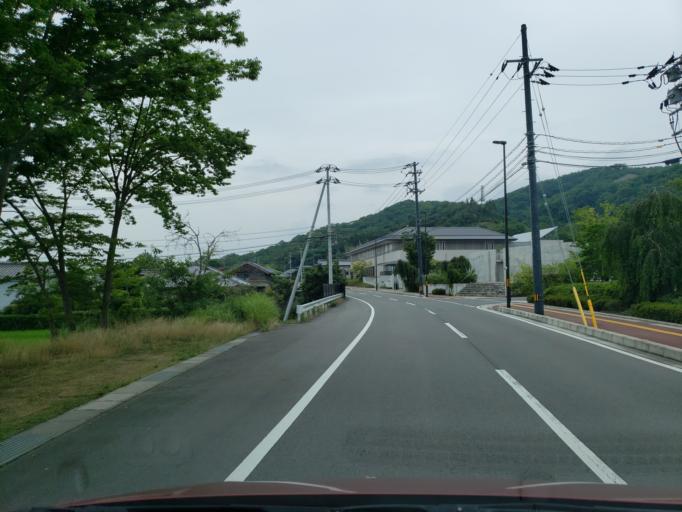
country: JP
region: Tokushima
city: Kamojimacho-jogejima
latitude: 34.1015
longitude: 134.2966
